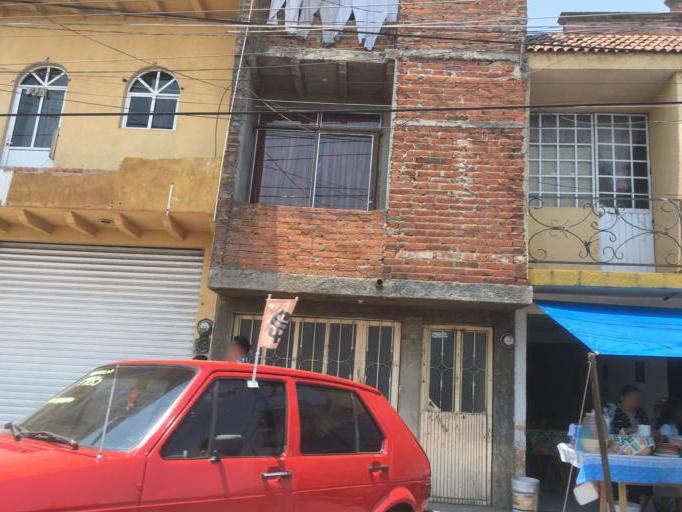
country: MX
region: Michoacan
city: Quiroga
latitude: 19.6640
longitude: -101.5276
